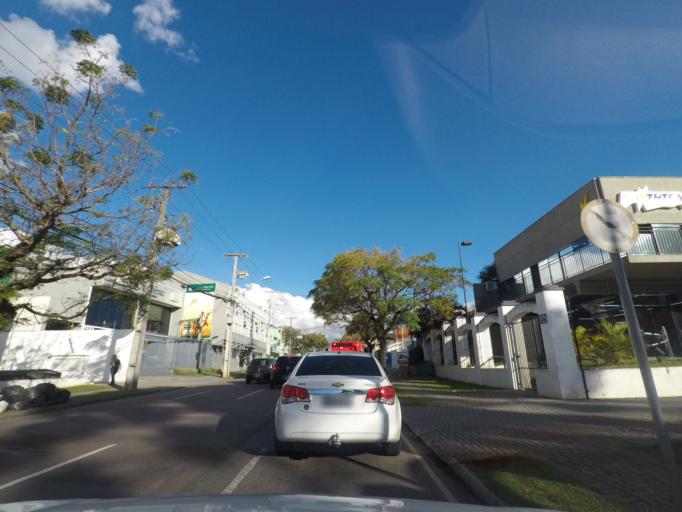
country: BR
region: Parana
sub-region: Curitiba
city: Curitiba
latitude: -25.4507
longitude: -49.2646
